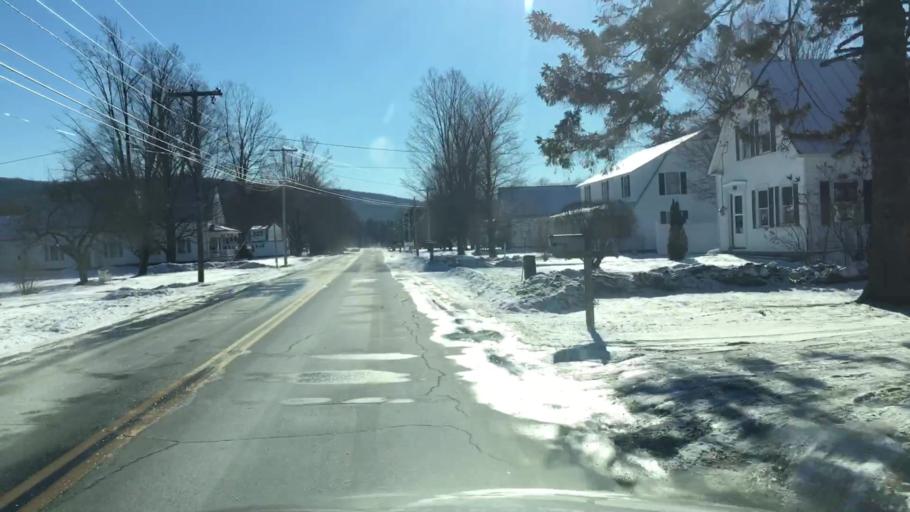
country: US
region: New Hampshire
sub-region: Grafton County
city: Woodsville
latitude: 44.2581
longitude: -72.0526
